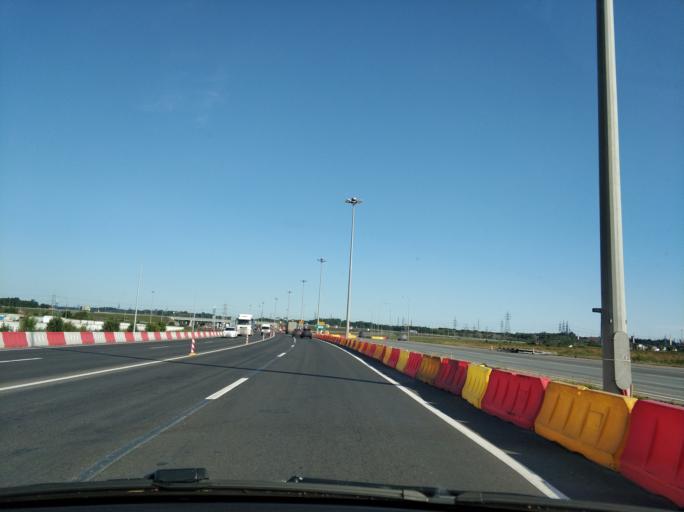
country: RU
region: Leningrad
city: Bugry
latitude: 60.0876
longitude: 30.3752
